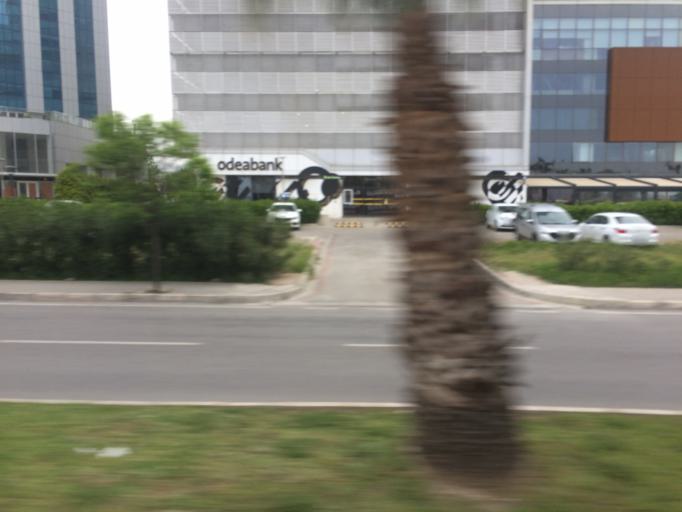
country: TR
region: Izmir
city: Izmir
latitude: 38.4566
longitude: 27.1671
